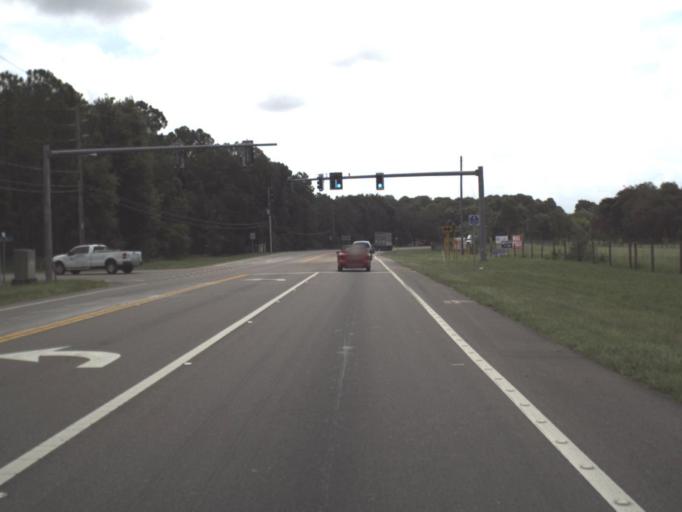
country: US
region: Florida
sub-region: Pasco County
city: Shady Hills
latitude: 28.3304
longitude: -82.5424
